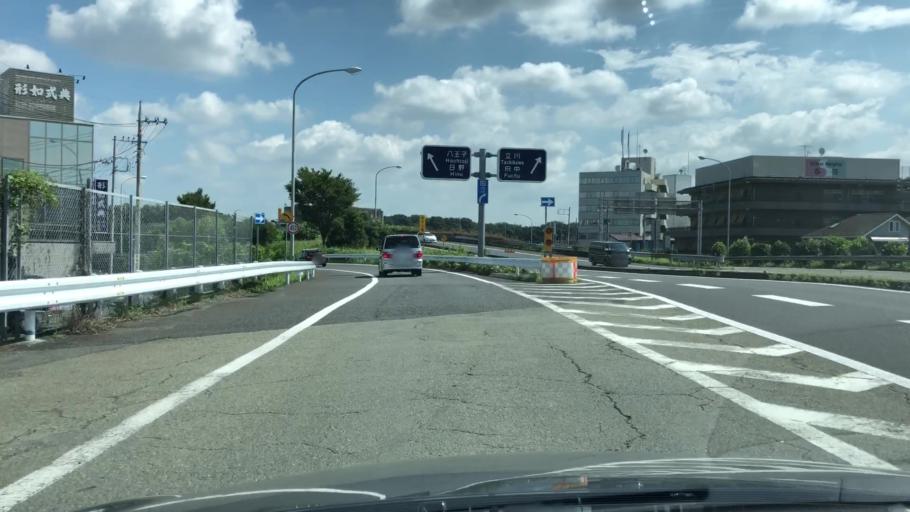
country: JP
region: Tokyo
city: Hino
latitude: 35.6745
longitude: 139.4427
